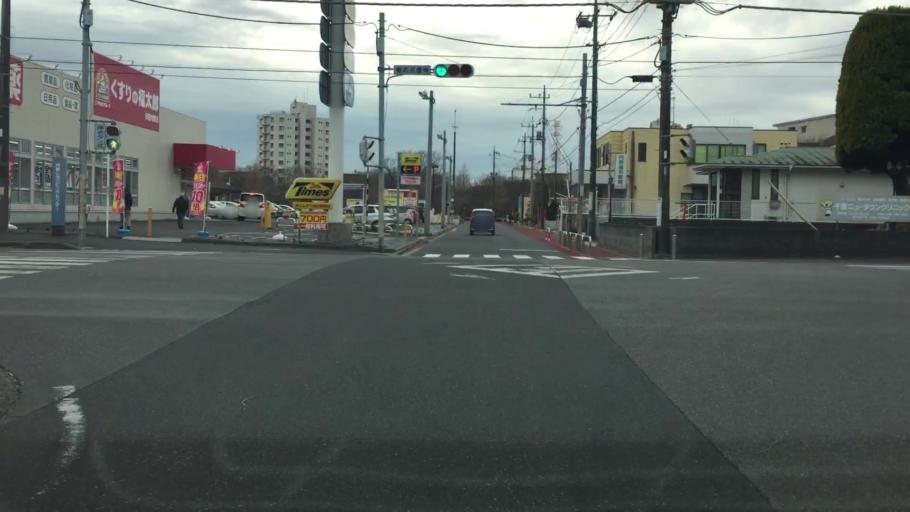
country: JP
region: Chiba
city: Shiroi
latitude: 35.7978
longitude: 140.1279
